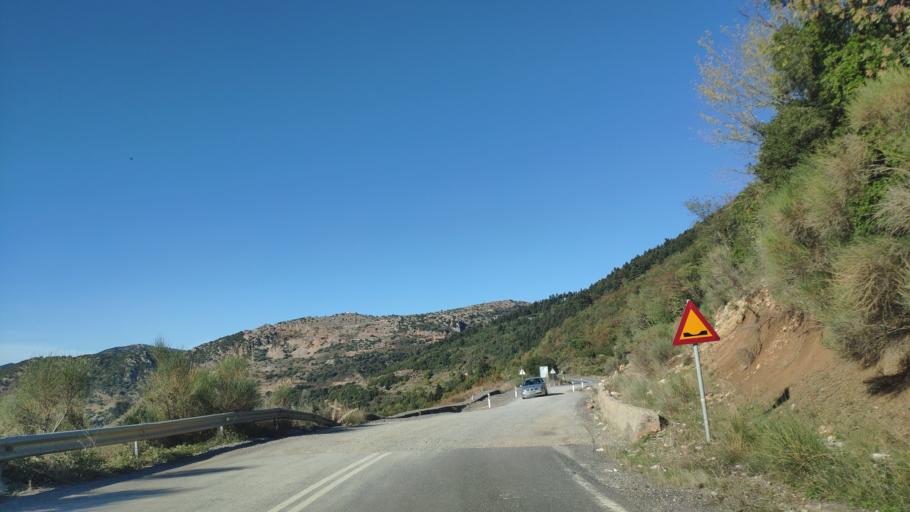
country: GR
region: Peloponnese
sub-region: Nomos Arkadias
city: Dimitsana
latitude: 37.5677
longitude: 22.0603
